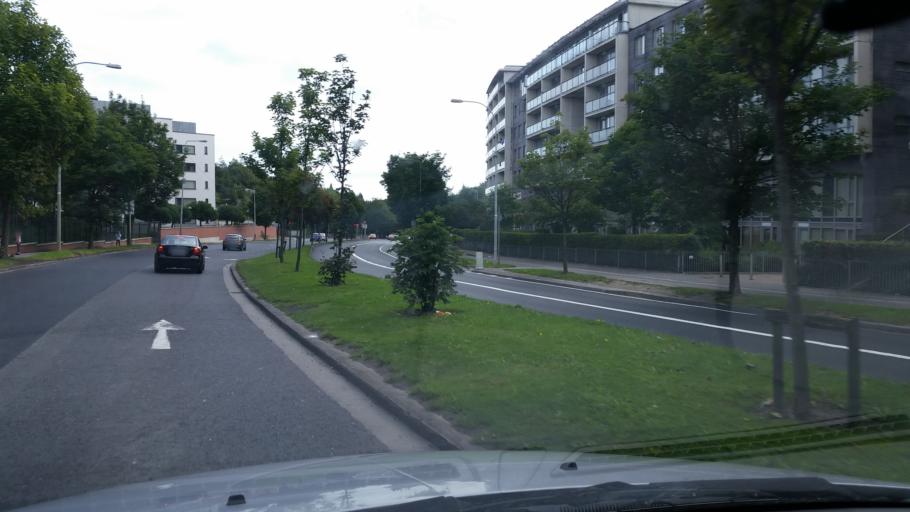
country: IE
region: Leinster
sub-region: Dublin City
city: Finglas
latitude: 53.3812
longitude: -6.2896
